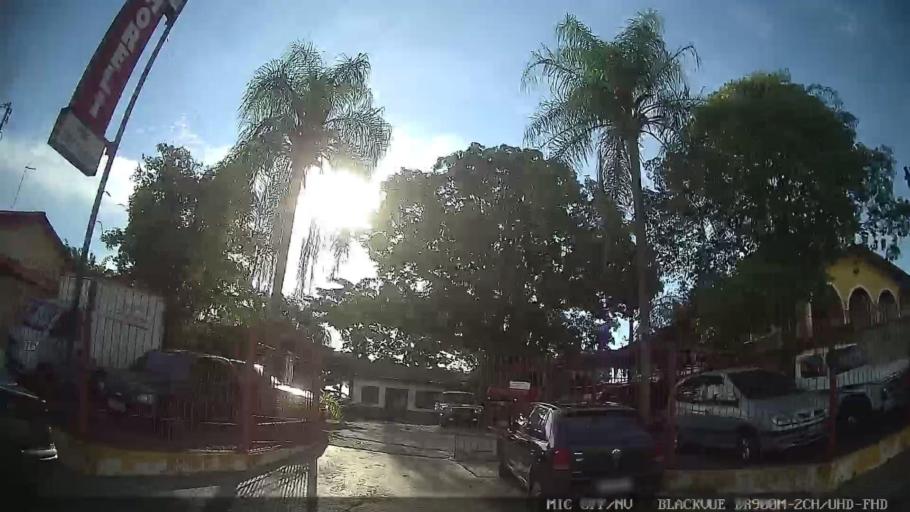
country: BR
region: Sao Paulo
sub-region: Tiete
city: Tiete
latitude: -23.1145
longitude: -47.7111
